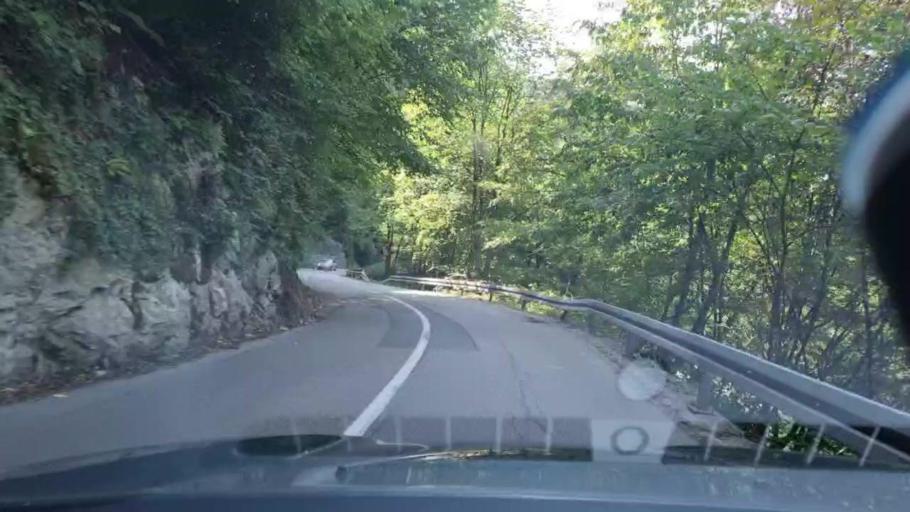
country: BA
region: Federation of Bosnia and Herzegovina
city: Bosanska Krupa
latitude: 44.8649
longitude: 16.0925
